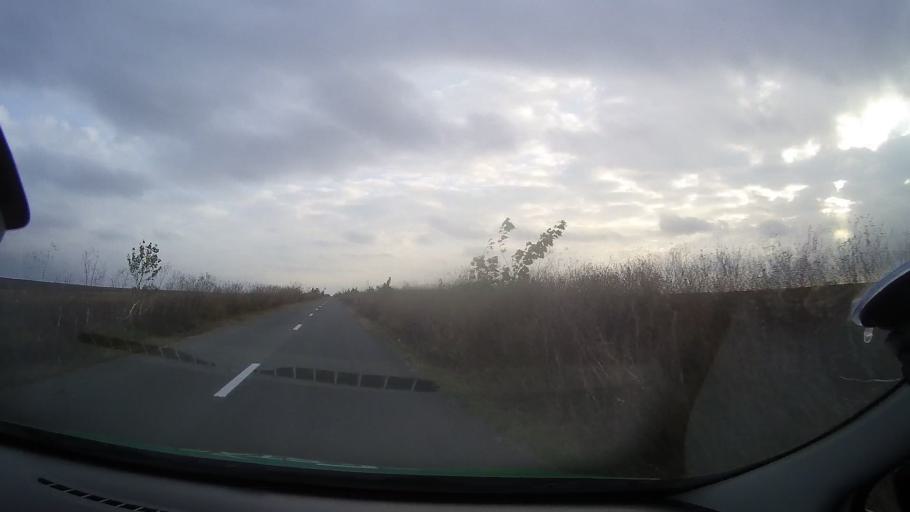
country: RO
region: Constanta
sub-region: Comuna Pestera
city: Pestera
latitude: 44.1439
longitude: 28.1160
